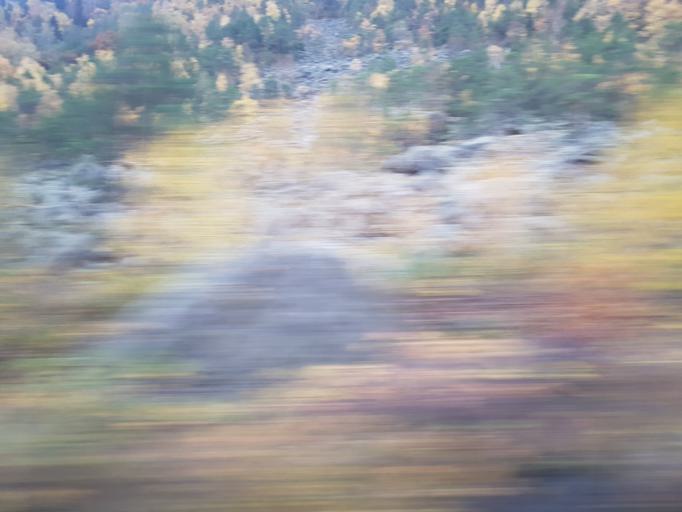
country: NO
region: Oppland
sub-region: Sel
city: Otta
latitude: 61.8396
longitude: 9.4636
